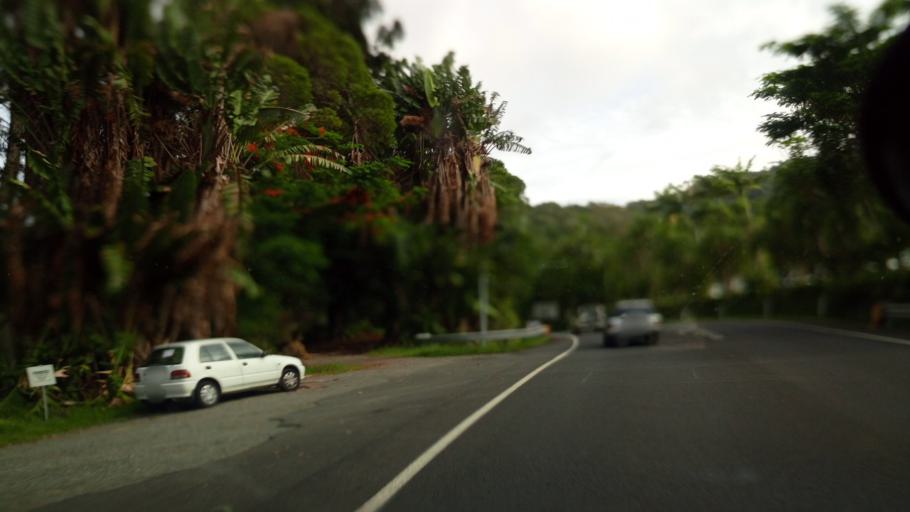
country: AU
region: Queensland
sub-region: Tablelands
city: Kuranda
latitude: -16.8255
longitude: 145.6511
